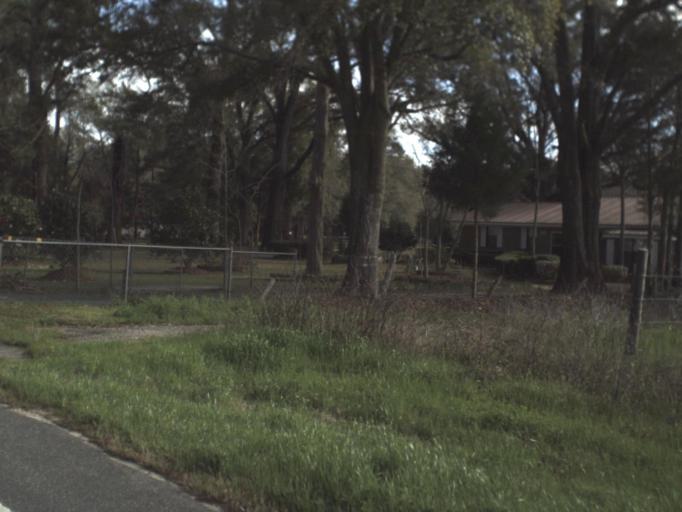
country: US
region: Florida
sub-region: Jackson County
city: Marianna
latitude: 30.8310
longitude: -85.1673
